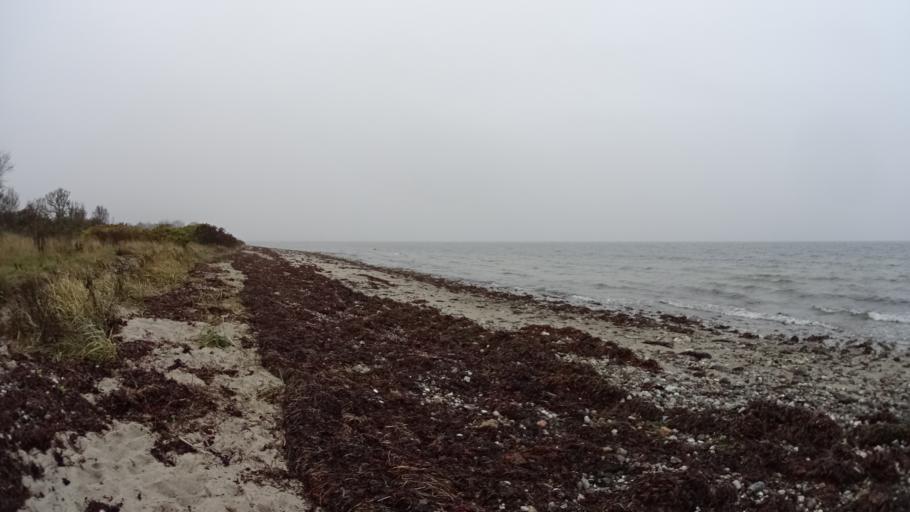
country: DK
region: Central Jutland
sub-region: Odder Kommune
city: Odder
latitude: 55.9358
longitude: 10.2601
